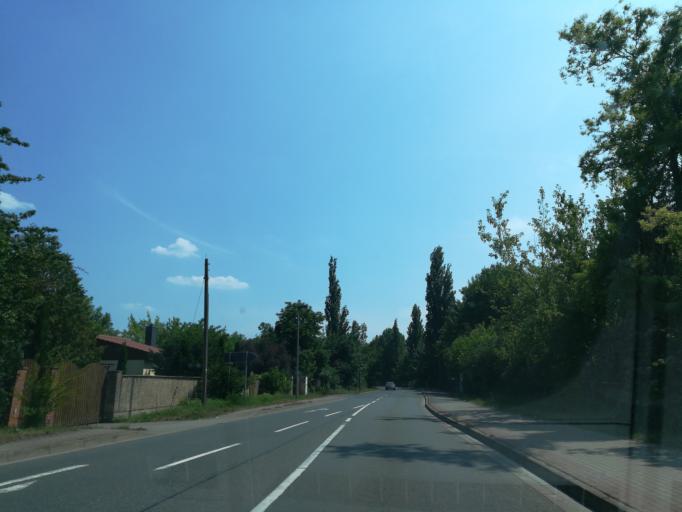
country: DE
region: Saxony-Anhalt
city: Aschersleben
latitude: 51.7706
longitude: 11.4496
